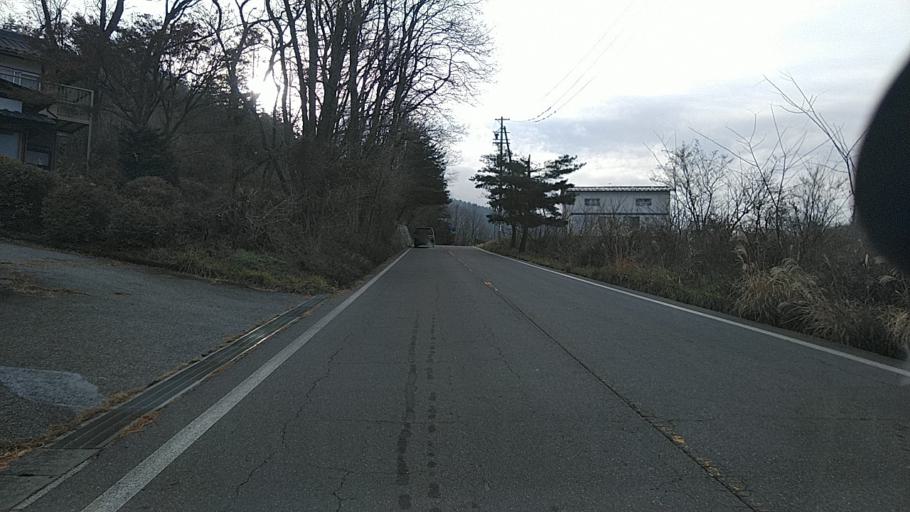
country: JP
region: Nagano
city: Matsumoto
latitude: 36.1685
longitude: 137.9960
